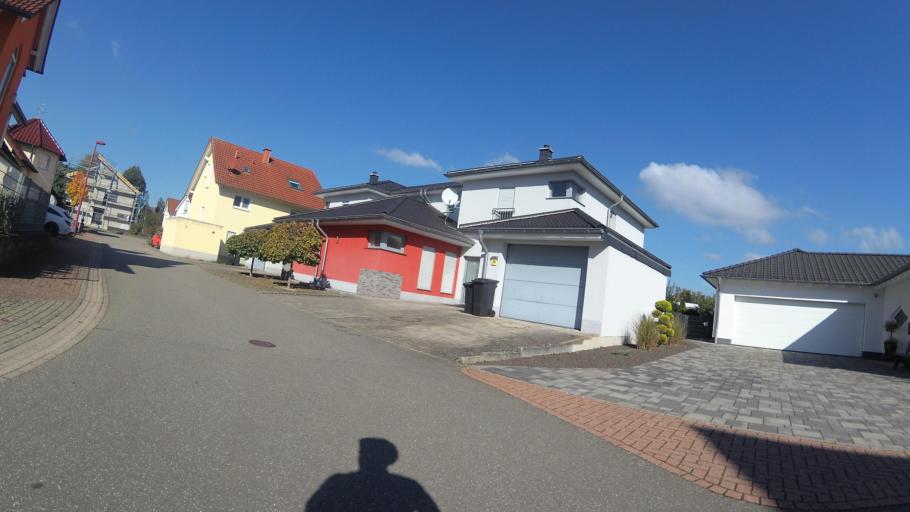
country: DE
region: Rheinland-Pfalz
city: Waldmohr
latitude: 49.3816
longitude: 7.3319
